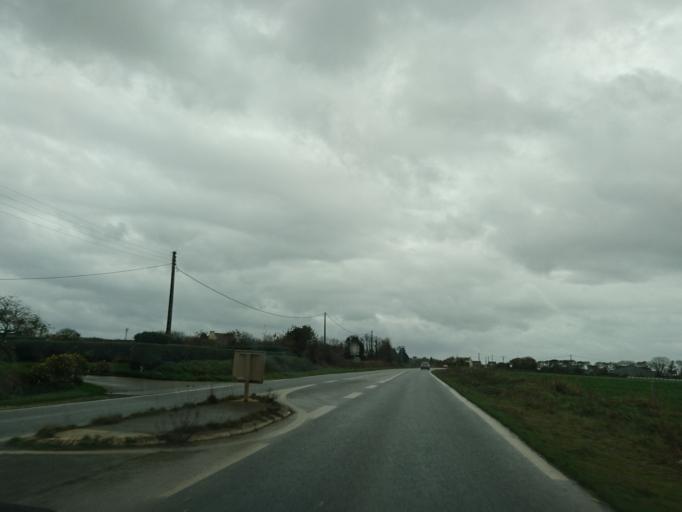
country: FR
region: Brittany
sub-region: Departement du Finistere
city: Plouzane
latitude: 48.3623
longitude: -4.6049
